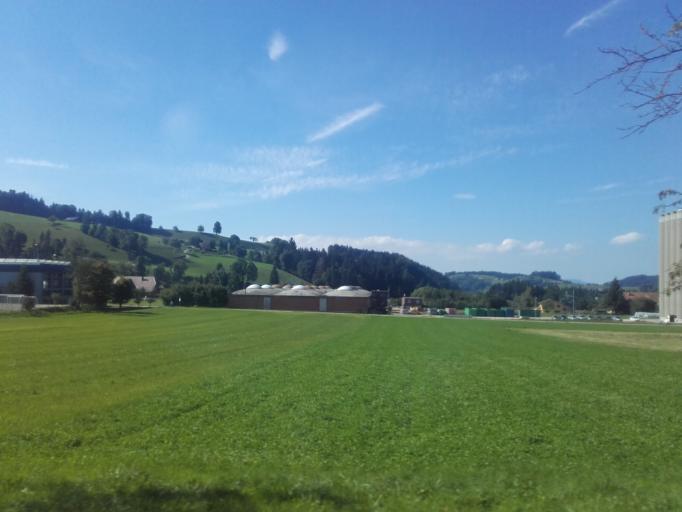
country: CH
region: Bern
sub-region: Oberaargau
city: Huttwil
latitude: 47.1100
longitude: 7.8325
